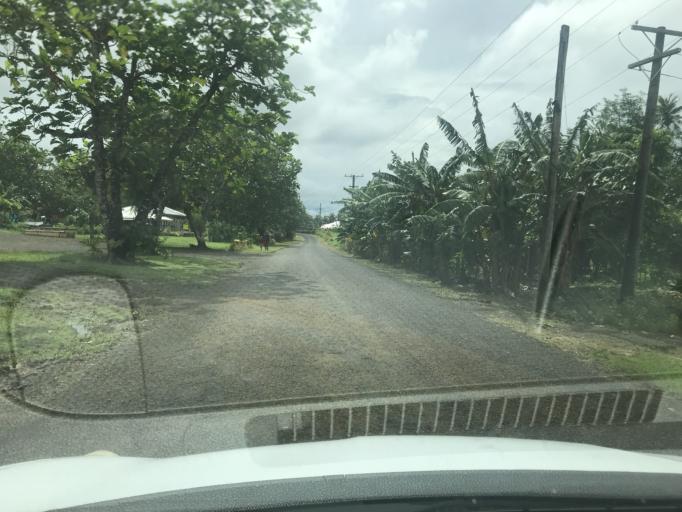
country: WS
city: Matavai
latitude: -14.0324
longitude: -171.6299
